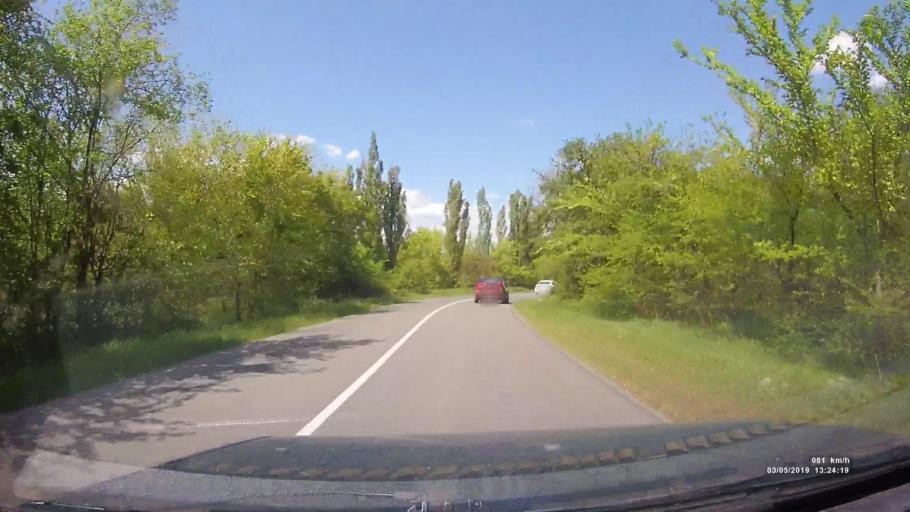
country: RU
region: Rostov
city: Semikarakorsk
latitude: 47.5642
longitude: 40.7955
